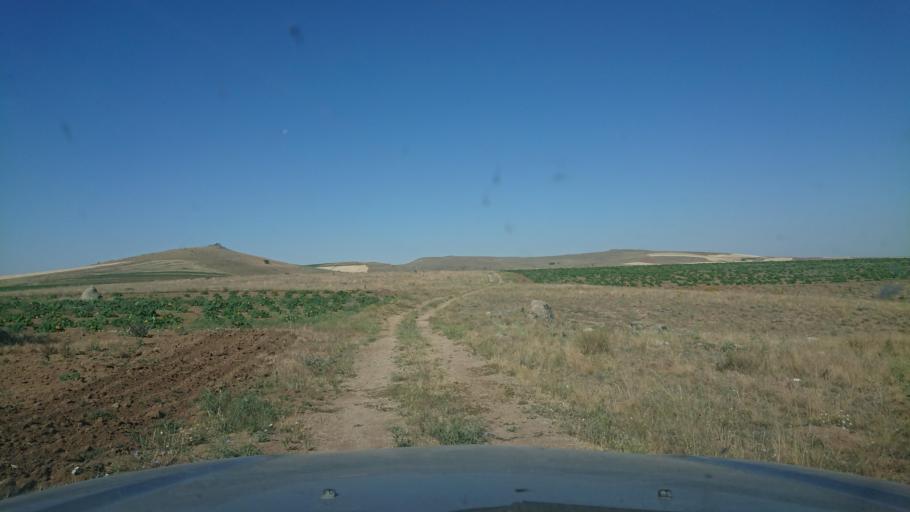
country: TR
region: Aksaray
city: Agacoren
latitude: 38.8379
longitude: 33.9397
